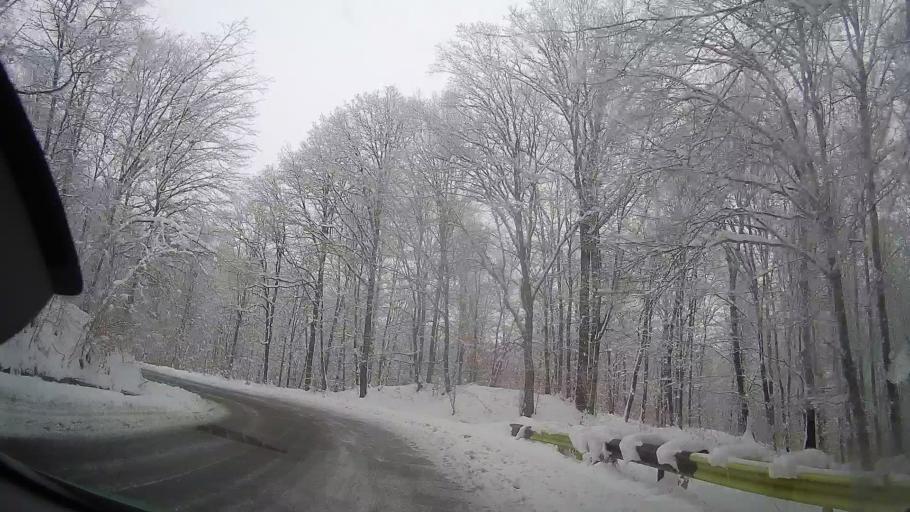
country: RO
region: Neamt
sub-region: Comuna Valea Ursului
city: Valea Ursului
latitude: 46.8476
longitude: 27.0655
